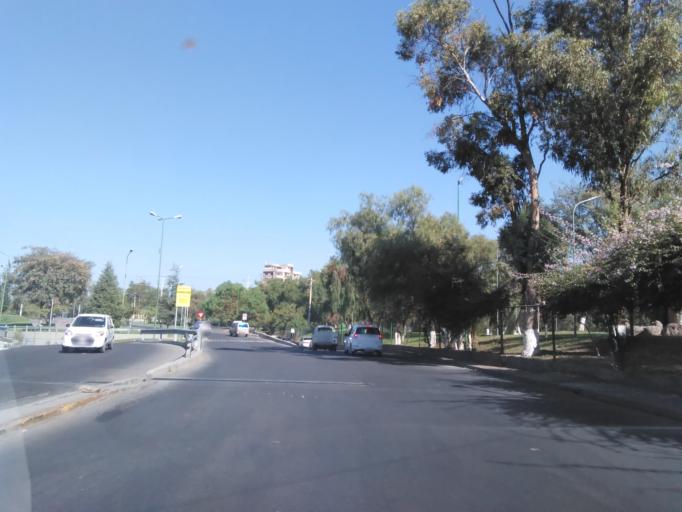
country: BO
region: Cochabamba
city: Cochabamba
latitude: -17.3871
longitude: -66.1633
